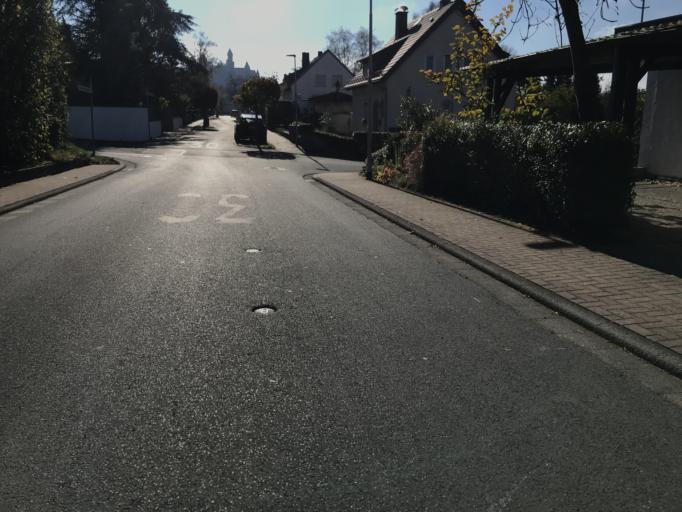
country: DE
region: Hesse
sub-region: Regierungsbezirk Giessen
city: Braunfels
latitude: 50.5217
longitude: 8.3838
